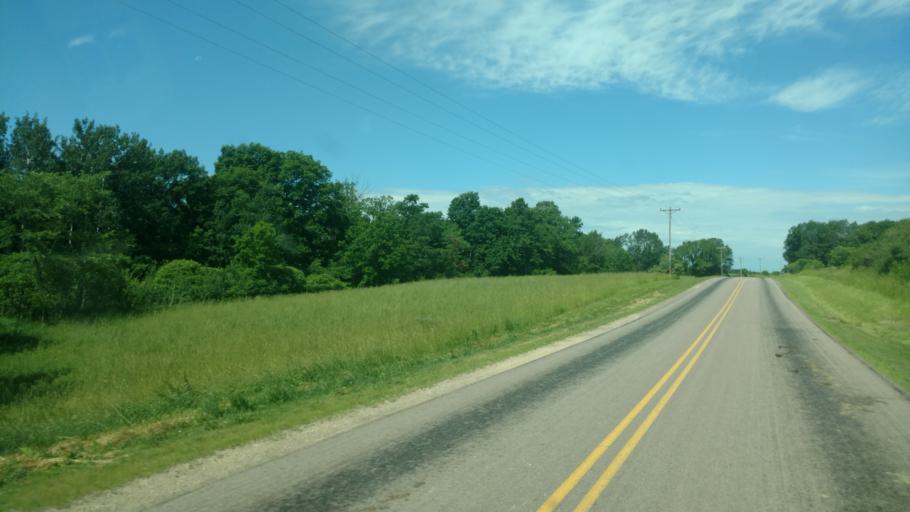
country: US
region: Wisconsin
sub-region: Vernon County
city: Hillsboro
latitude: 43.5920
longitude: -90.3883
